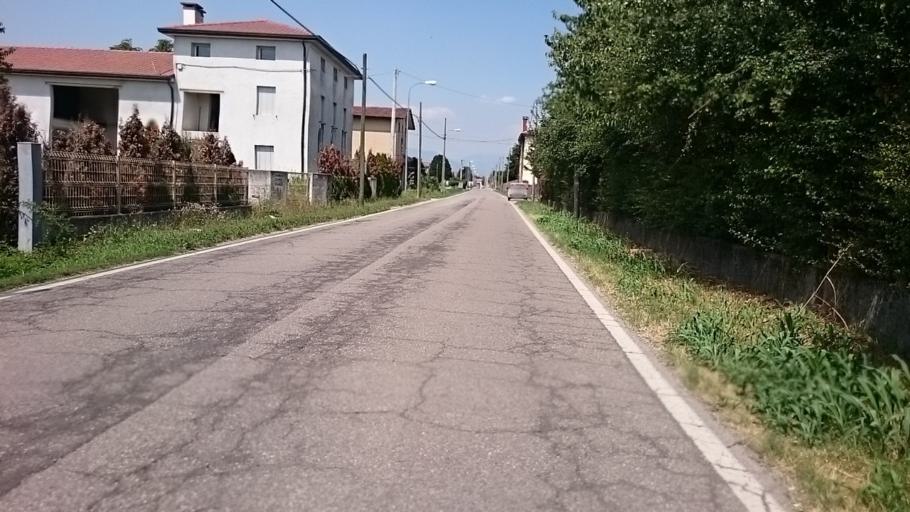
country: IT
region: Veneto
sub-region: Provincia di Padova
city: Fontaniva
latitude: 45.6558
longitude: 11.7581
